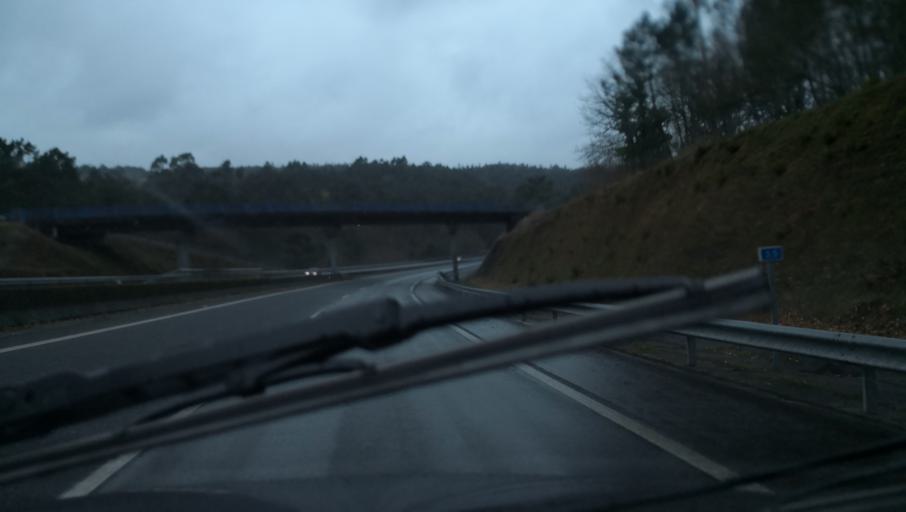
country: ES
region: Galicia
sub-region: Provincia da Coruna
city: Santiago de Compostela
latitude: 42.8274
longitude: -8.5219
